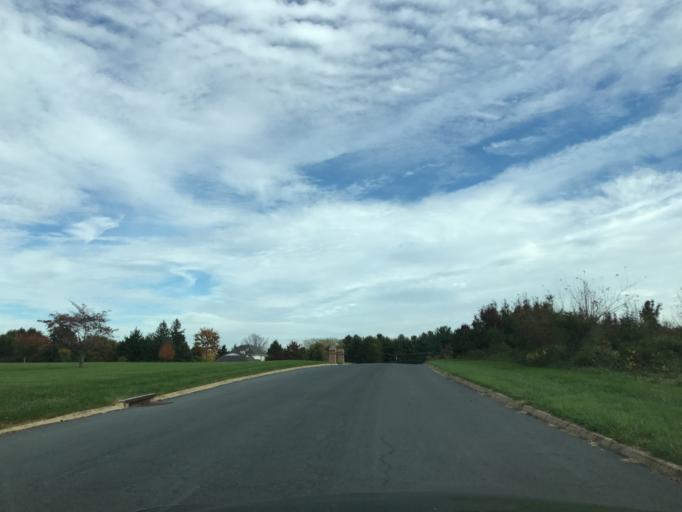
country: US
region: Maryland
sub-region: Harford County
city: Pleasant Hills
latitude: 39.4834
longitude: -76.3770
